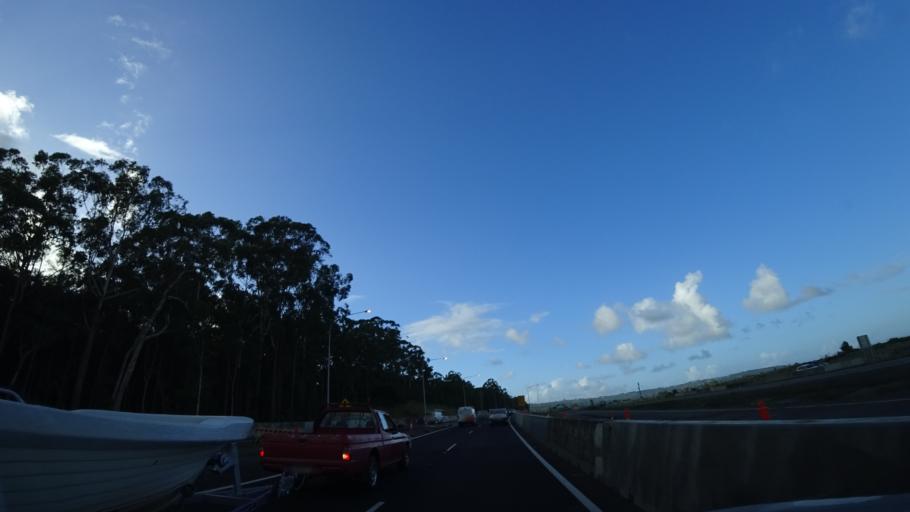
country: AU
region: Queensland
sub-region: Sunshine Coast
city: Buderim
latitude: -26.7415
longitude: 153.0474
